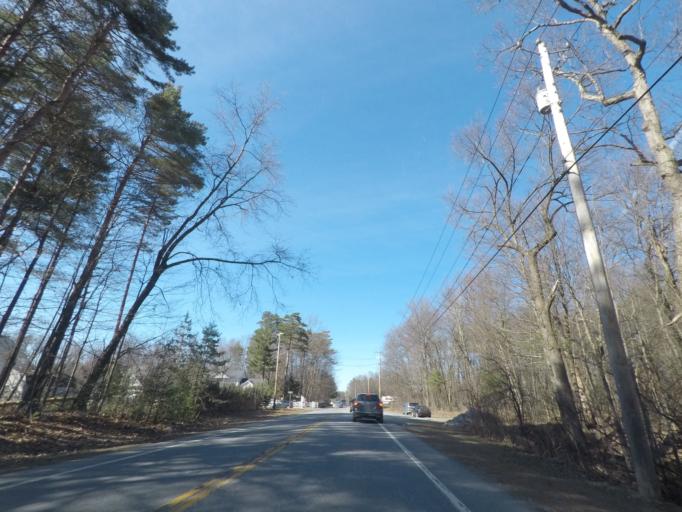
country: US
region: New York
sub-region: Saratoga County
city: Milton
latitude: 43.0306
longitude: -73.8483
